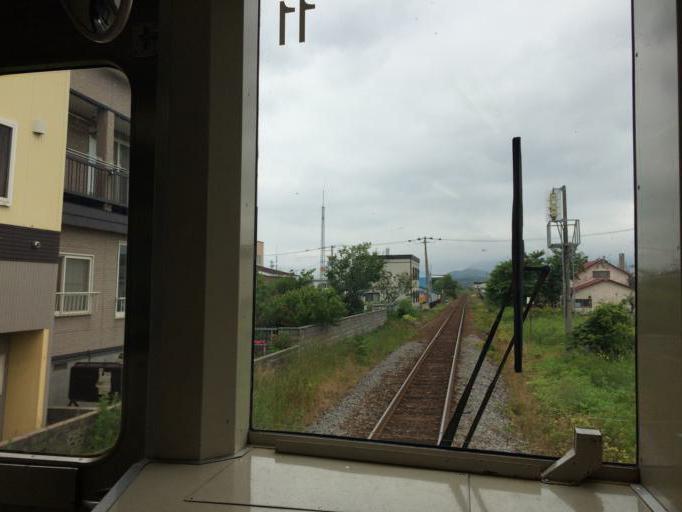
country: JP
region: Hokkaido
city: Yoichi
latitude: 43.1918
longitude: 140.8003
